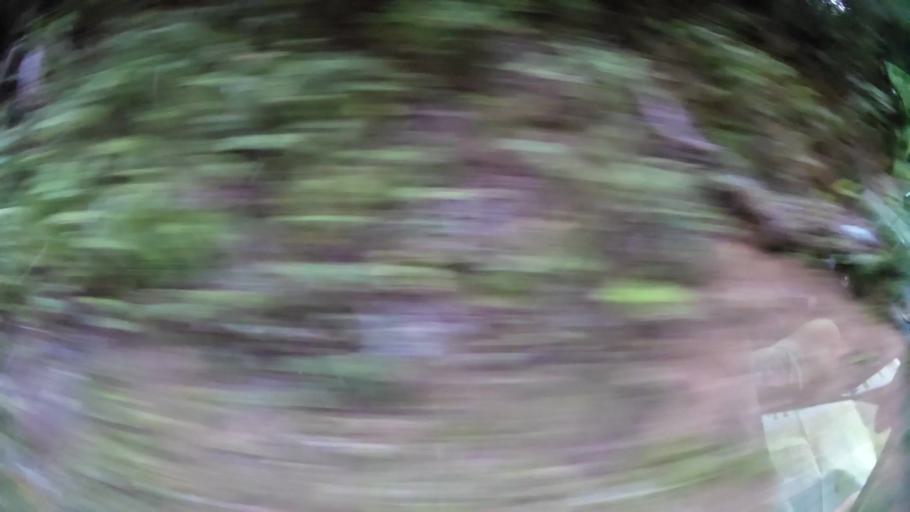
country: DM
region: Saint John
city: Portsmouth
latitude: 15.5847
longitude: -61.4139
